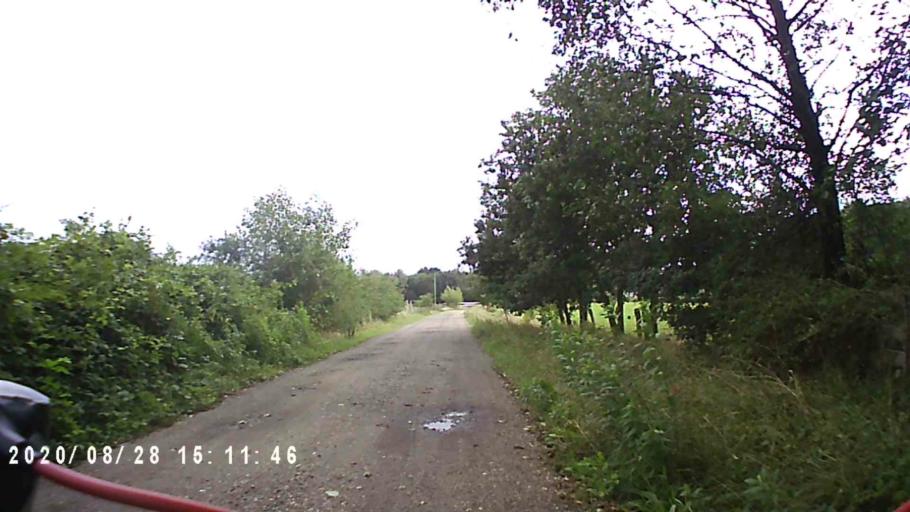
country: NL
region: Drenthe
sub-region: Gemeente Tynaarlo
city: Vries
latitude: 53.1277
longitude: 6.5738
